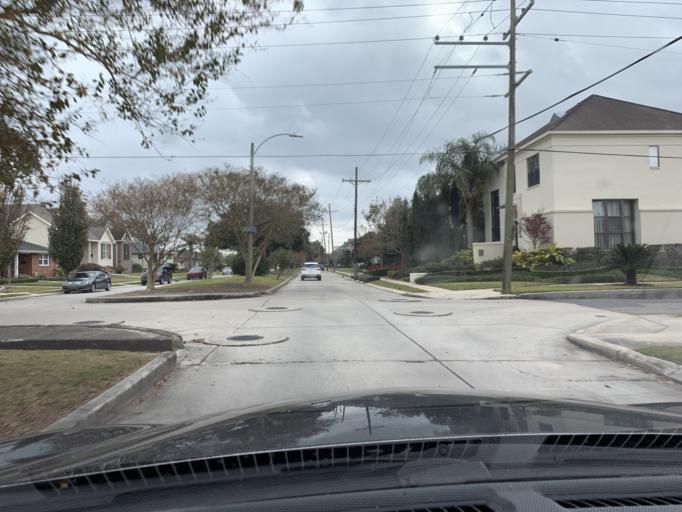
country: US
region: Louisiana
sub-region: Jefferson Parish
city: Metairie
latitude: 30.0174
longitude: -90.1013
